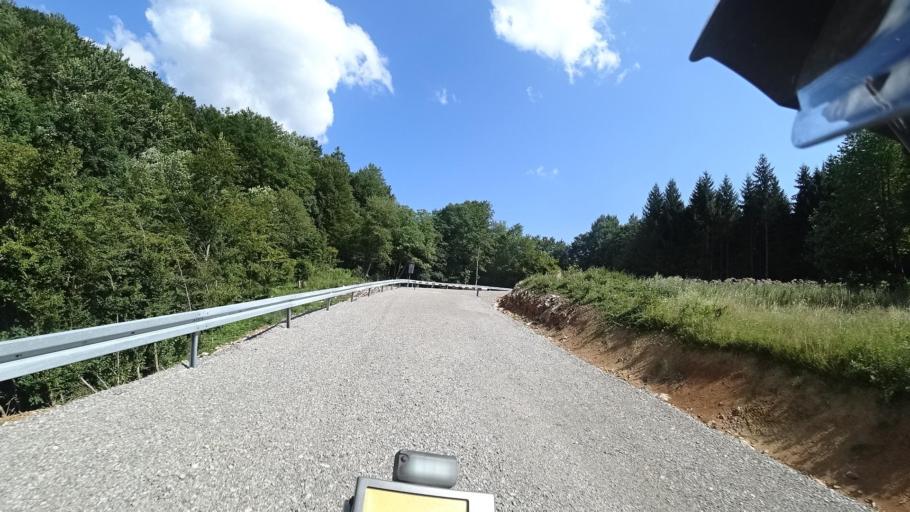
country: HR
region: Licko-Senjska
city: Brinje
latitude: 45.1408
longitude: 15.1128
